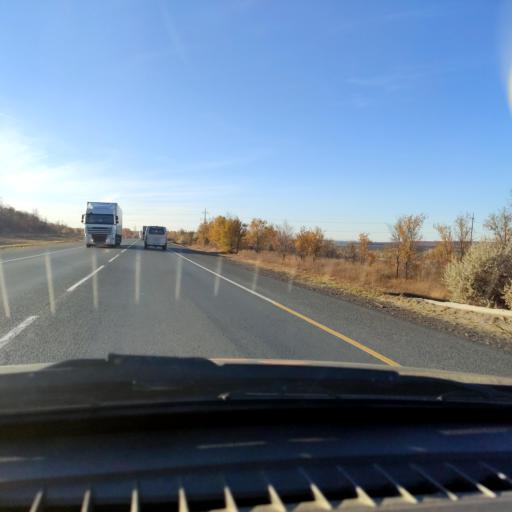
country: RU
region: Samara
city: Varlamovo
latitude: 53.1933
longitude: 48.3332
